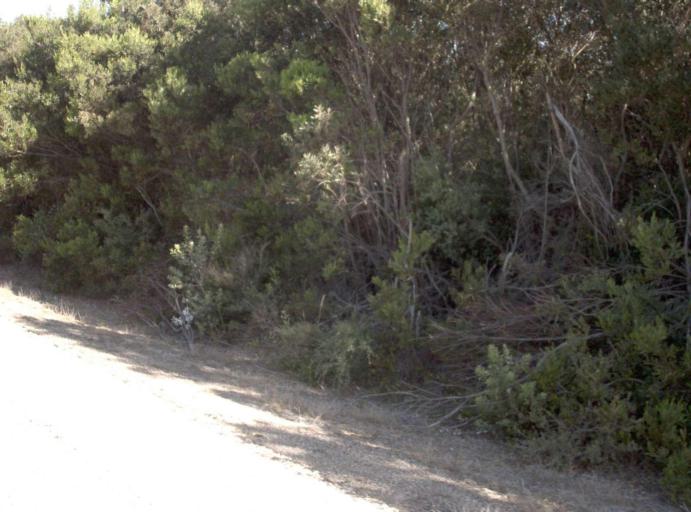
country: AU
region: Victoria
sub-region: East Gippsland
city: Lakes Entrance
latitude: -37.8018
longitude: 148.6194
